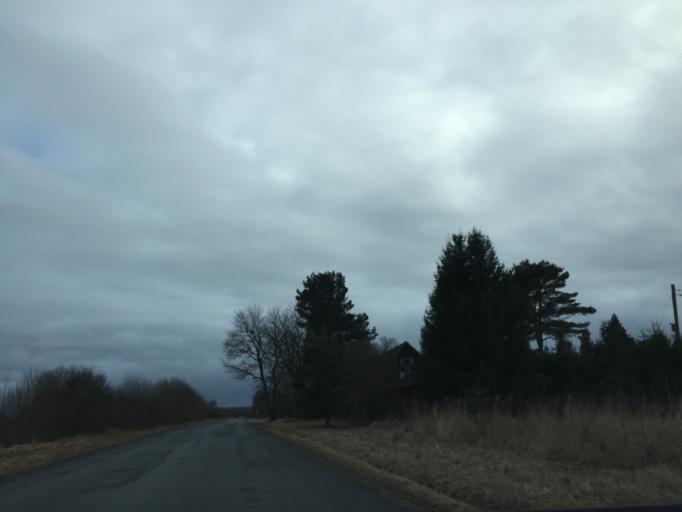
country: EE
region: Laeaene
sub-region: Haapsalu linn
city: Haapsalu
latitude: 58.8114
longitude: 23.5494
